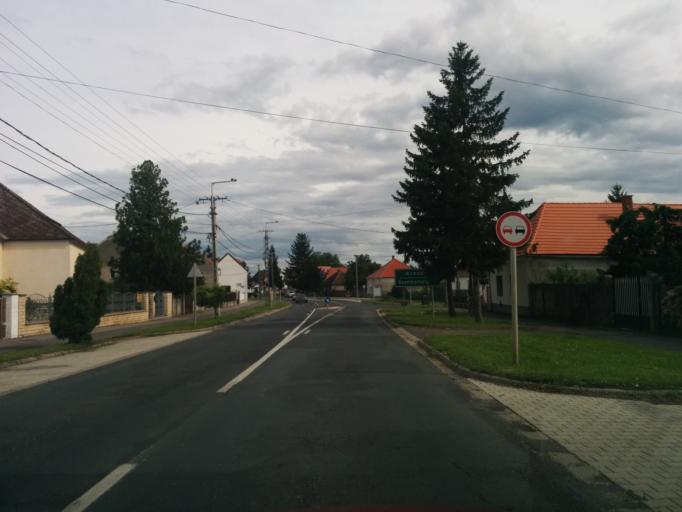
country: HU
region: Vas
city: Buk
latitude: 47.3774
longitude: 16.7610
